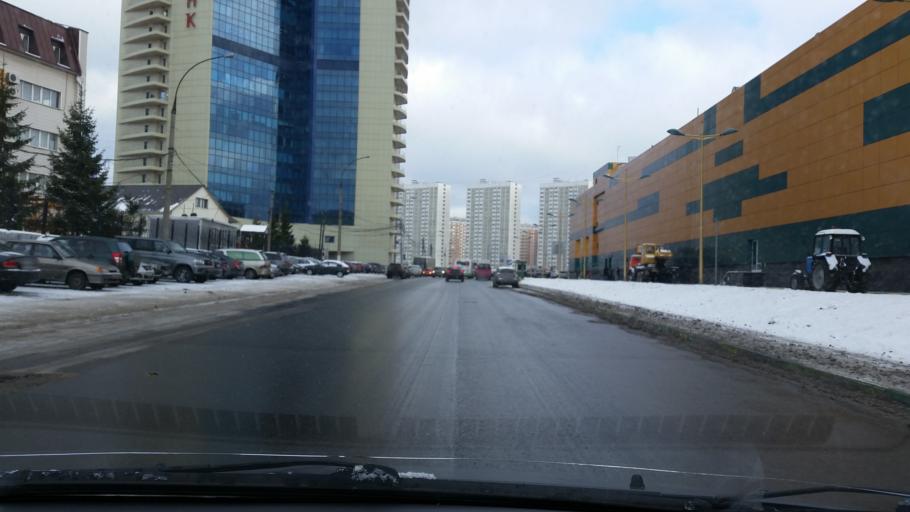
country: RU
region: Moscow
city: Vagonoremont
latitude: 55.9103
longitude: 37.5405
